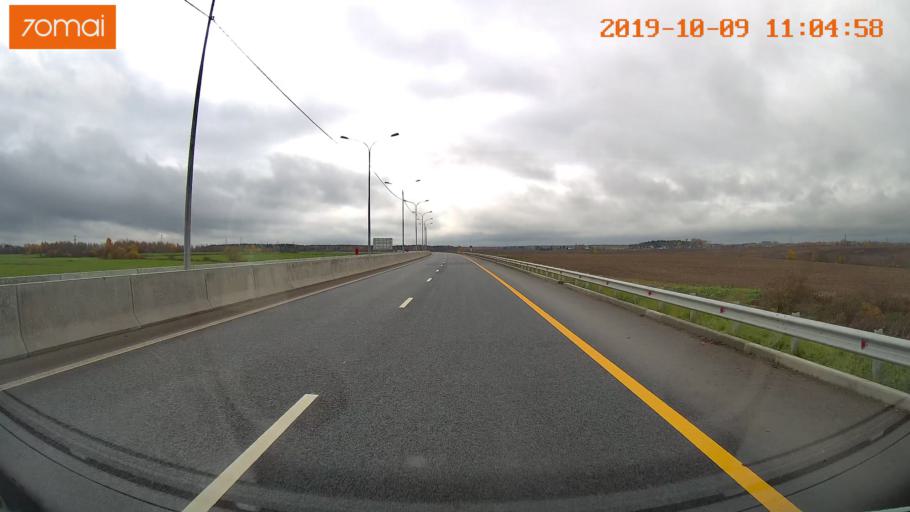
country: RU
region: Vologda
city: Molochnoye
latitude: 59.2057
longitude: 39.7614
